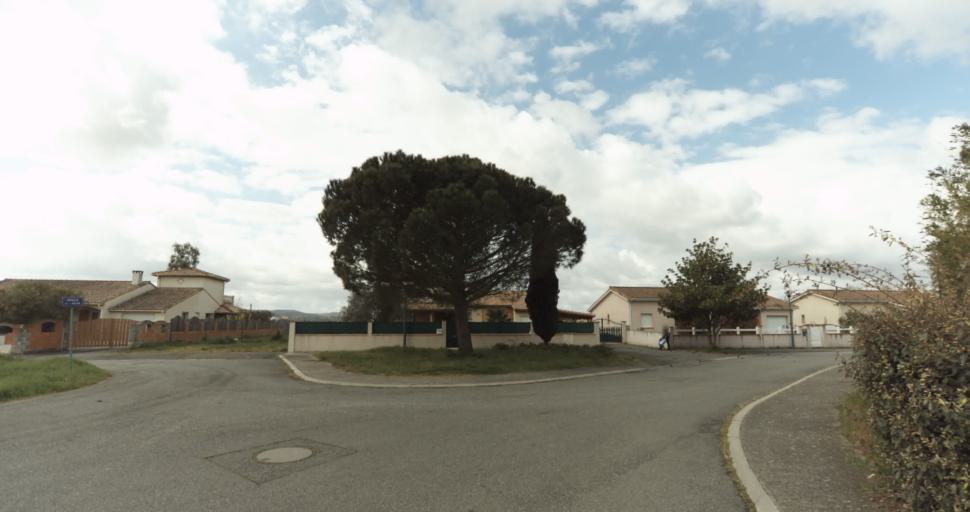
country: FR
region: Midi-Pyrenees
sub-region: Departement de la Haute-Garonne
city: Auterive
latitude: 43.3475
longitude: 1.4662
